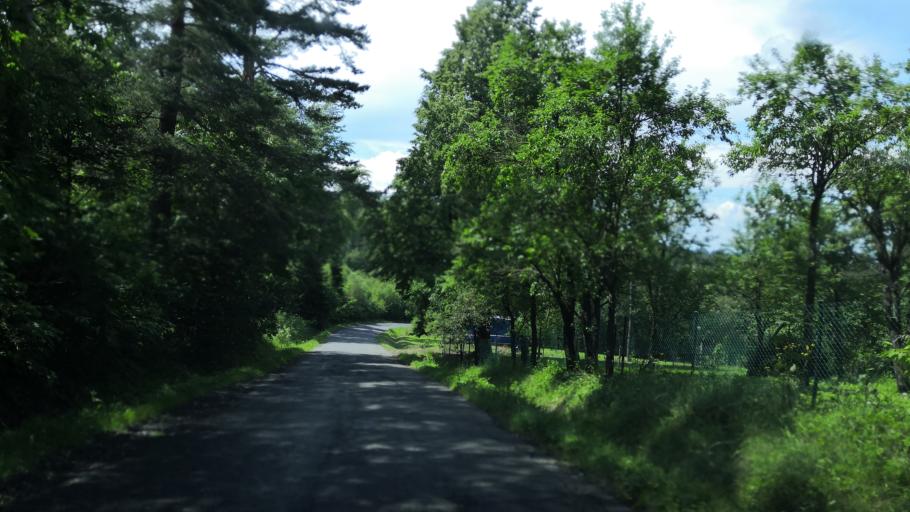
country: CZ
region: Zlin
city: Vidce
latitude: 49.4287
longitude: 18.0981
